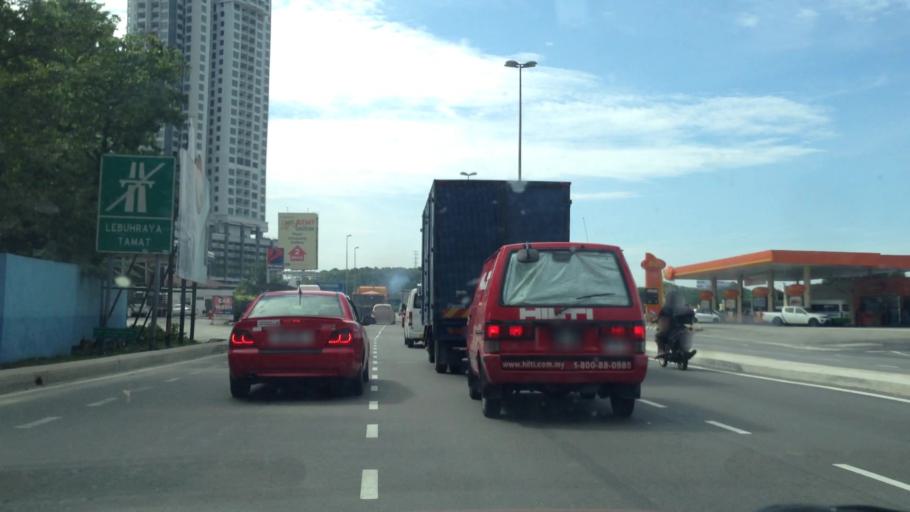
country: MY
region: Selangor
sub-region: Petaling
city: Petaling Jaya
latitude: 3.0834
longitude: 101.6626
